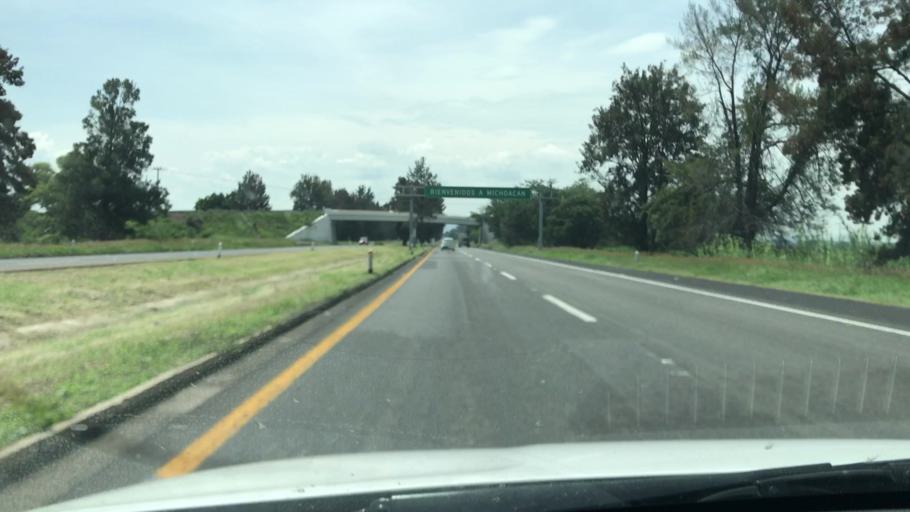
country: MX
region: Michoacan
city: Vistahermosa de Negrete
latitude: 20.3040
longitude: -102.4872
